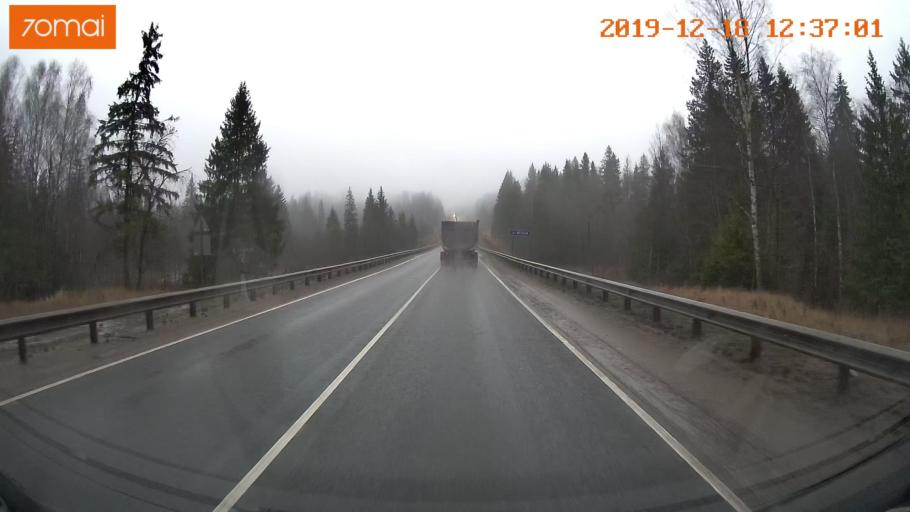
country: RU
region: Moskovskaya
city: Rumyantsevo
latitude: 56.1415
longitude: 36.5985
